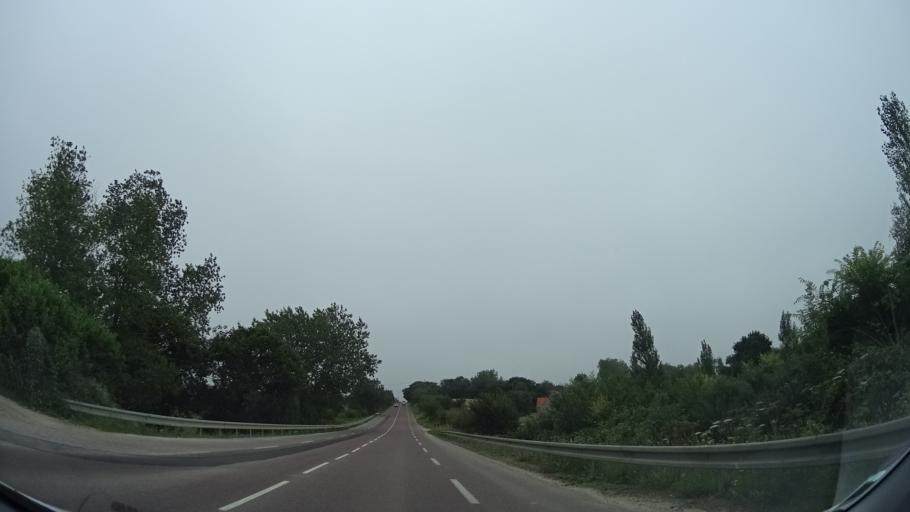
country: FR
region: Lower Normandy
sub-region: Departement de la Manche
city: Flamanville
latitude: 49.5398
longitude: -1.8363
